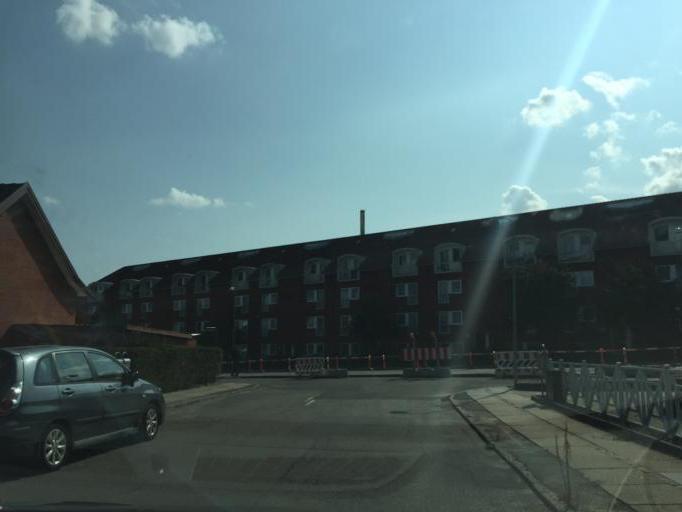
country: DK
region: South Denmark
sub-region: Odense Kommune
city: Odense
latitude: 55.3996
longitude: 10.3443
